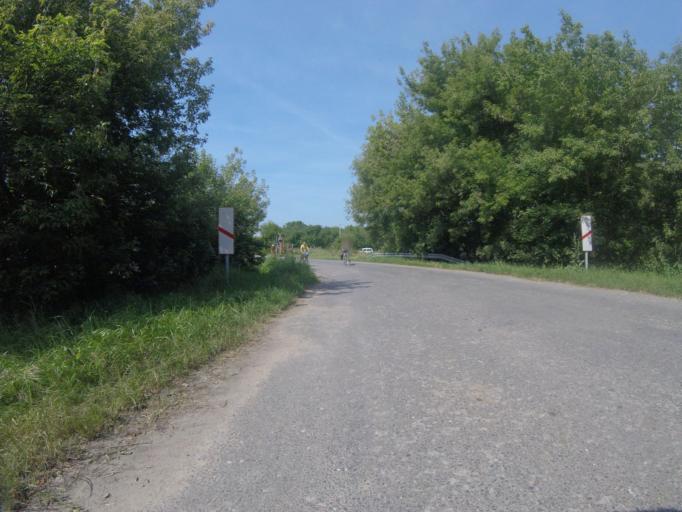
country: HU
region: Tolna
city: Bolcske
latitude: 46.7272
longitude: 18.9298
